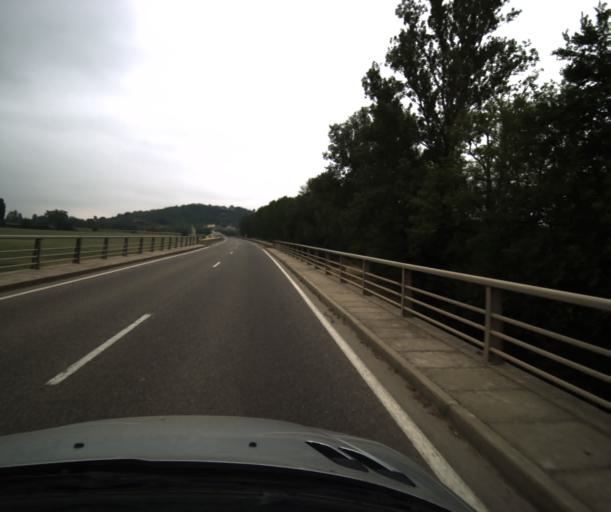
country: FR
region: Midi-Pyrenees
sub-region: Departement du Tarn-et-Garonne
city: Saint-Nicolas-de-la-Grave
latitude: 44.0799
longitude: 0.9926
